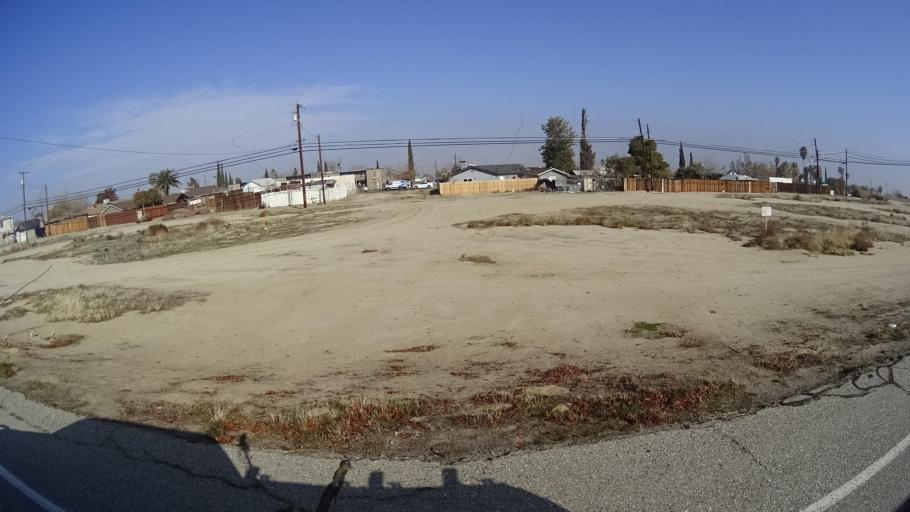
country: US
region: California
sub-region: Kern County
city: South Taft
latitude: 35.1379
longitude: -119.4529
